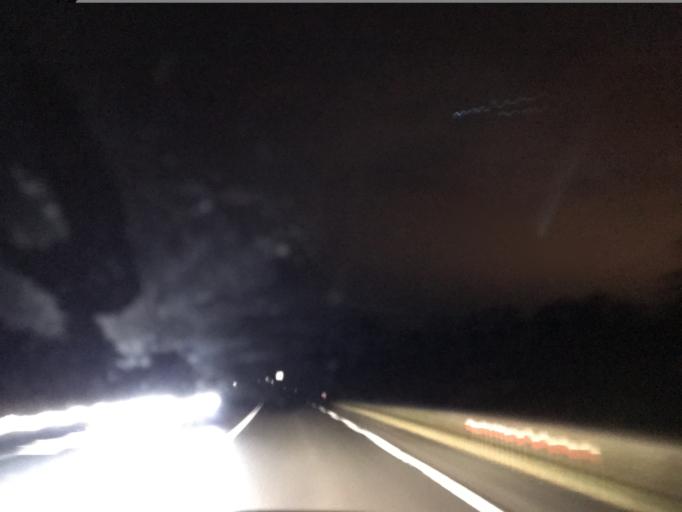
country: FR
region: Auvergne
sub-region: Departement de l'Allier
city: Hauterive
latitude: 46.0704
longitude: 3.4417
